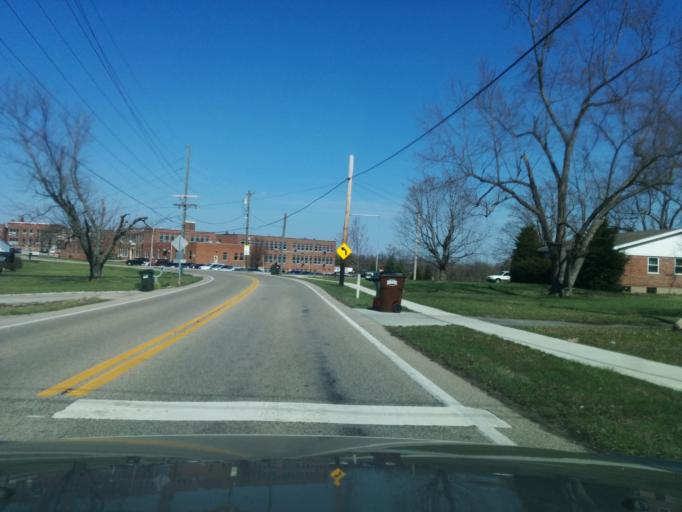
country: US
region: Ohio
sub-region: Hamilton County
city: Dry Ridge
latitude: 39.2371
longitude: -84.6135
